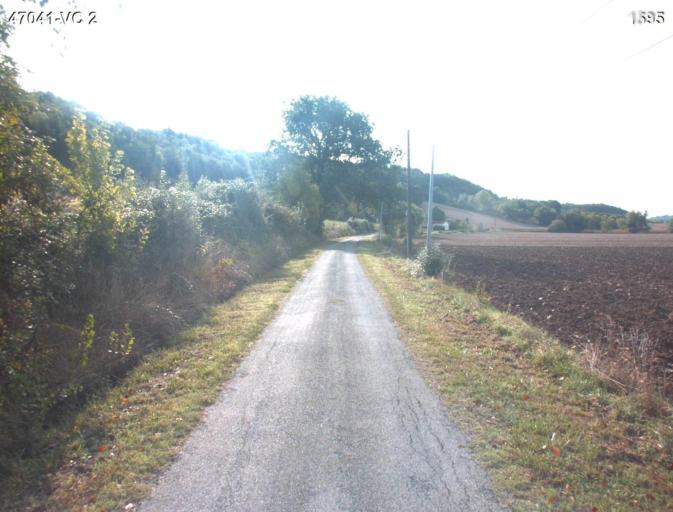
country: FR
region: Aquitaine
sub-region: Departement du Lot-et-Garonne
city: Port-Sainte-Marie
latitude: 44.1892
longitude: 0.4170
